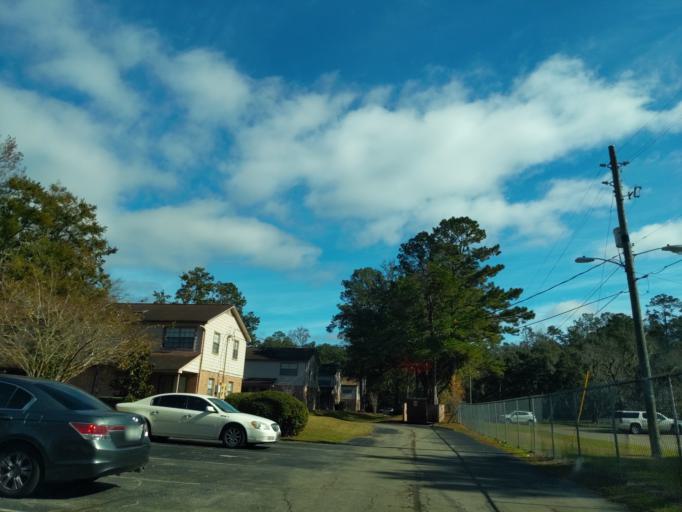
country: US
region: Florida
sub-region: Leon County
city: Tallahassee
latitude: 30.4770
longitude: -84.3225
